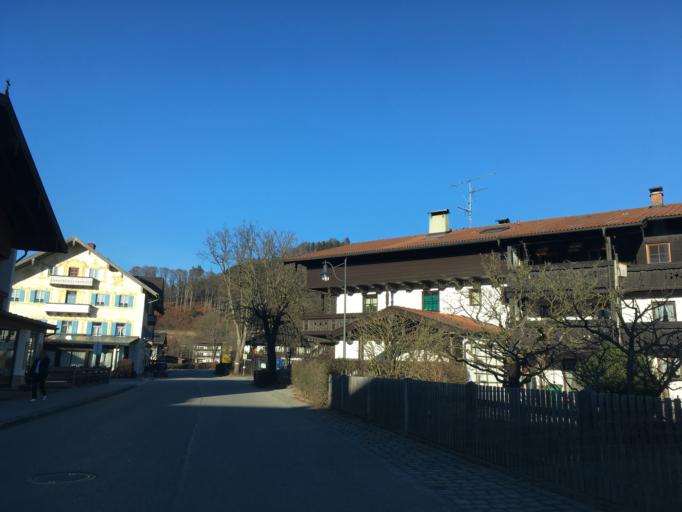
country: DE
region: Bavaria
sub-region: Upper Bavaria
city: Nussdorf am Inn
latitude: 47.7414
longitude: 12.1561
